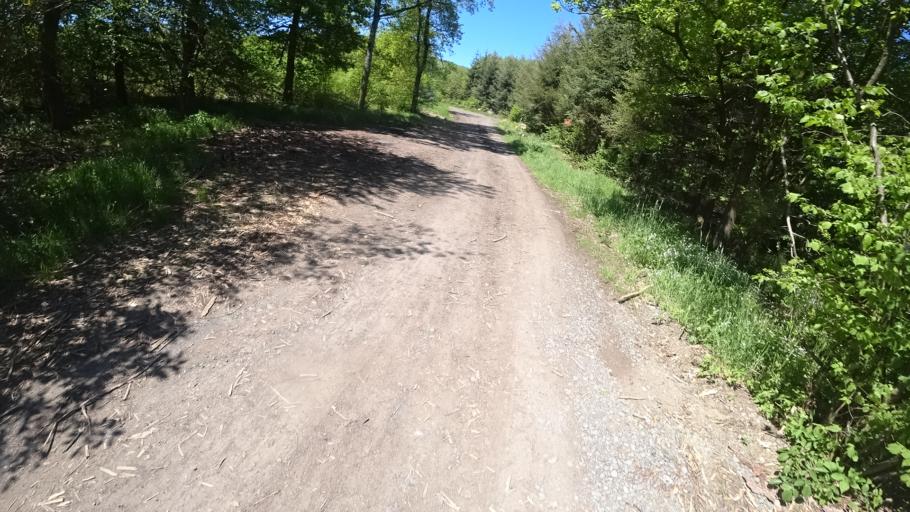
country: DE
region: Rheinland-Pfalz
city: Steineroth
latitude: 50.7537
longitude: 7.8597
